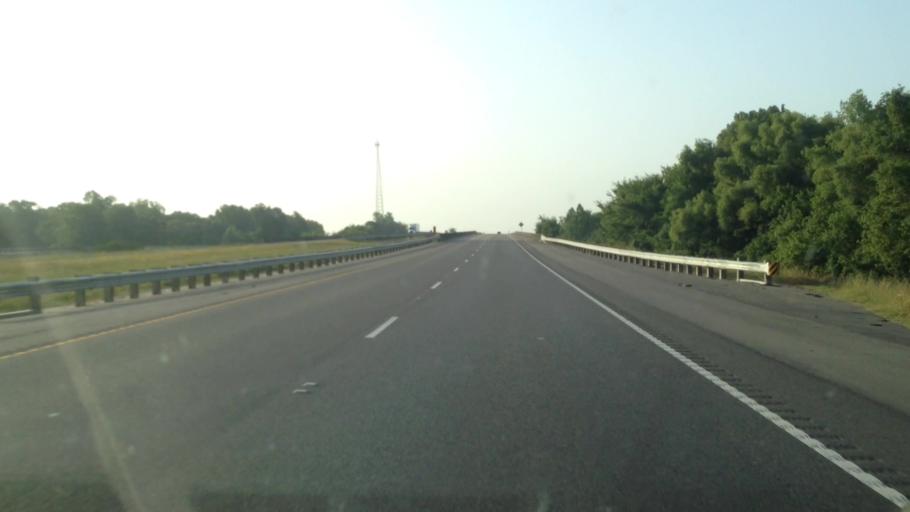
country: US
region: Louisiana
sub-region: Rapides Parish
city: Boyce
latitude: 31.3955
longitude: -92.6975
